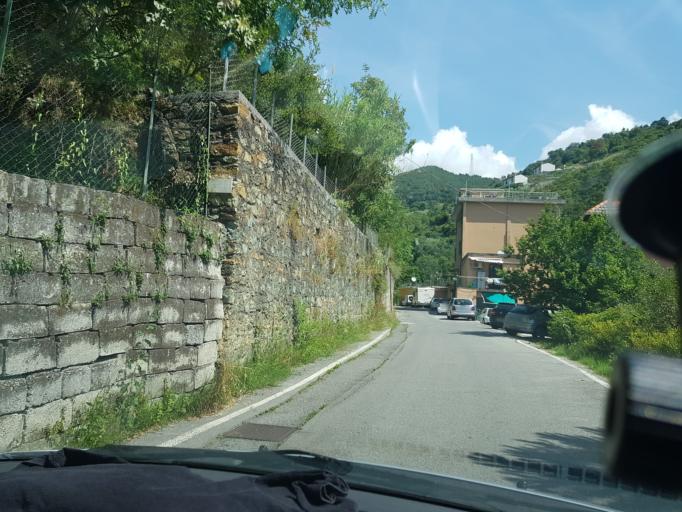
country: IT
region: Liguria
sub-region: Provincia di Genova
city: San Teodoro
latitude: 44.4368
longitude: 8.8403
